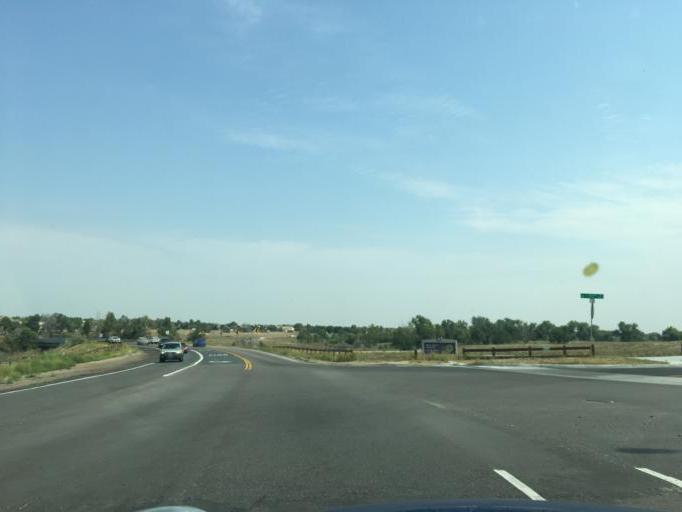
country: US
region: Colorado
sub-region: Adams County
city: Northglenn
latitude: 39.9208
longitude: -105.0136
